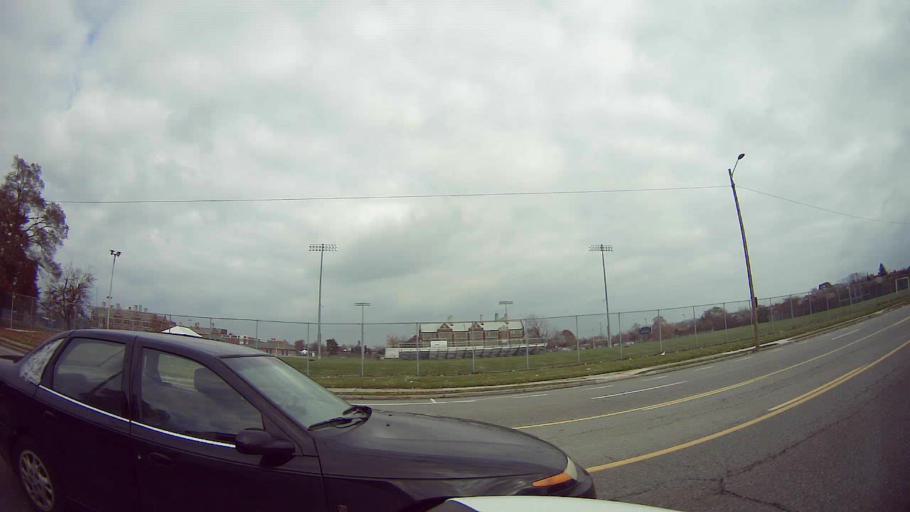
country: US
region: Michigan
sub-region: Wayne County
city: Highland Park
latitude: 42.3814
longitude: -83.1141
